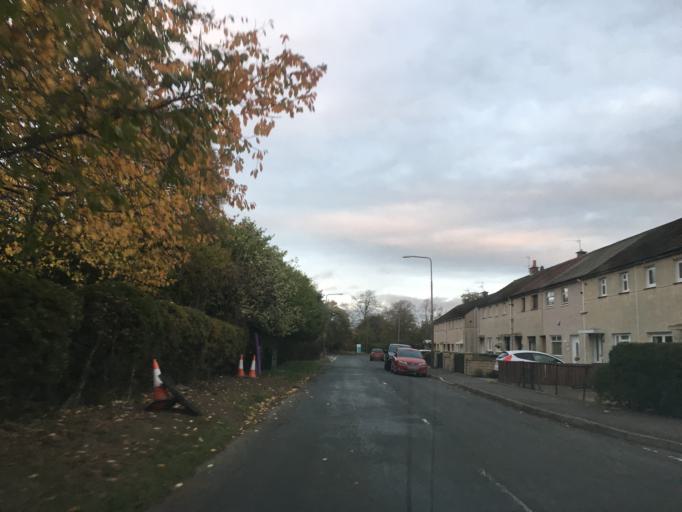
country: GB
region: Scotland
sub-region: Midlothian
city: Loanhead
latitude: 55.8719
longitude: -3.1798
